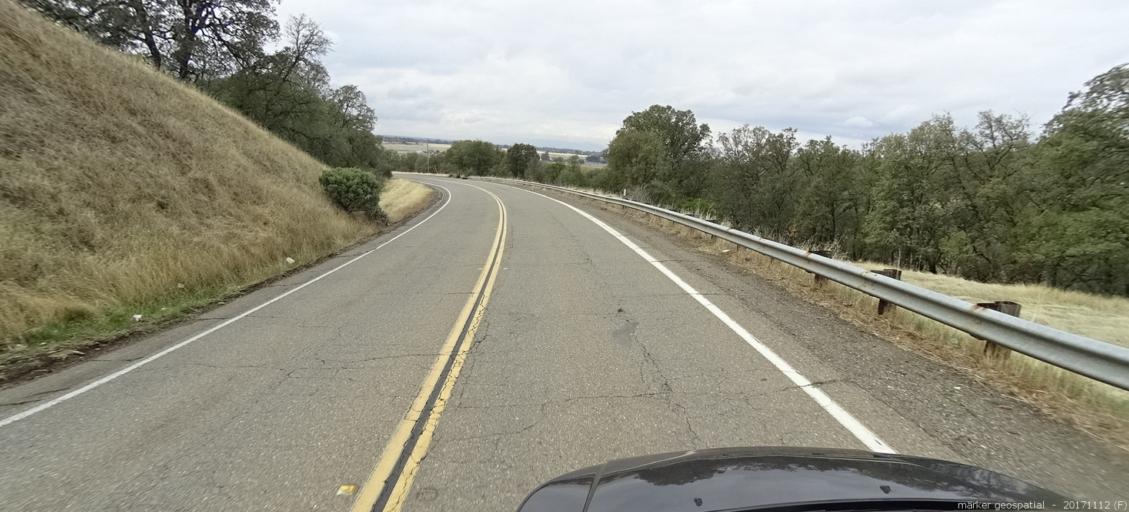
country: US
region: California
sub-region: Shasta County
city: Anderson
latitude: 40.4784
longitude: -122.2224
